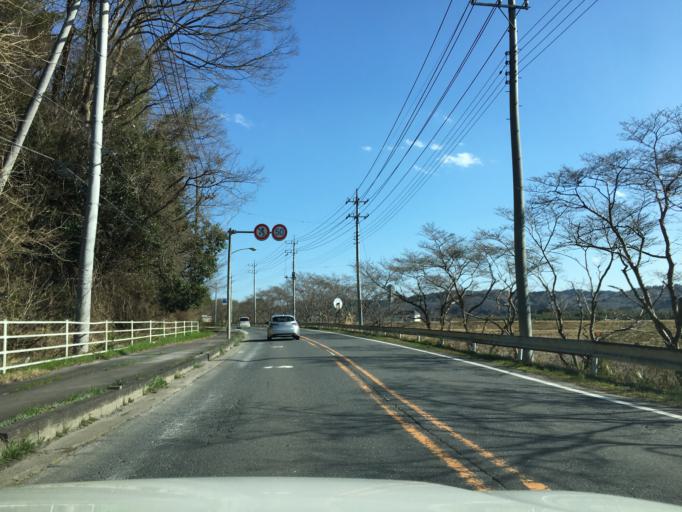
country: JP
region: Ibaraki
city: Omiya
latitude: 36.5650
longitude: 140.3033
